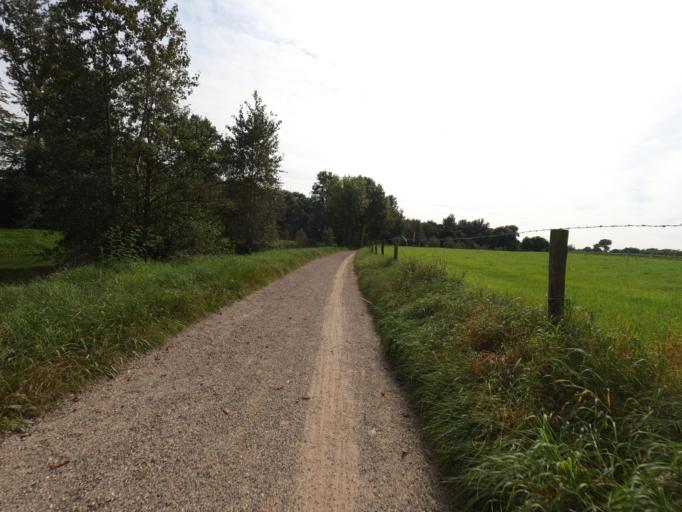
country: DE
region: North Rhine-Westphalia
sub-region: Regierungsbezirk Koln
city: Linnich
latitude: 51.0205
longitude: 6.2551
